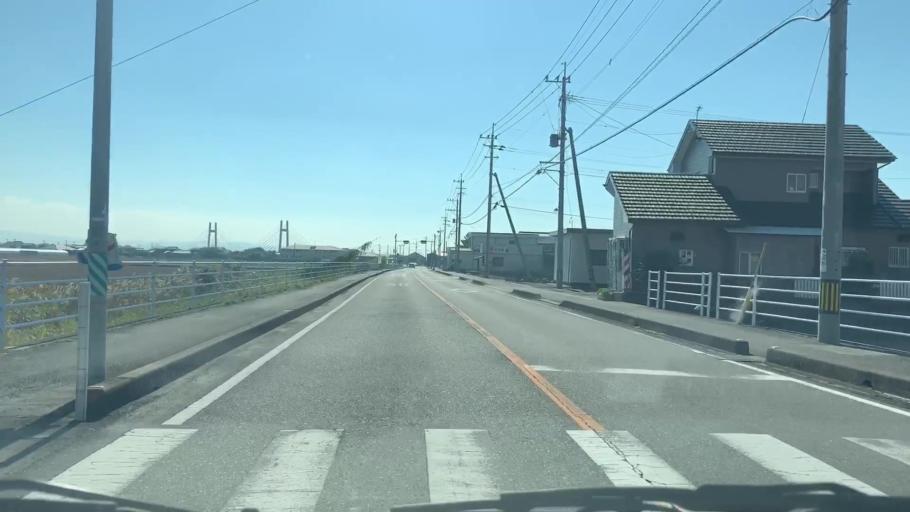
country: JP
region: Saga Prefecture
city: Kanzakimachi-kanzaki
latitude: 33.2937
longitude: 130.4450
